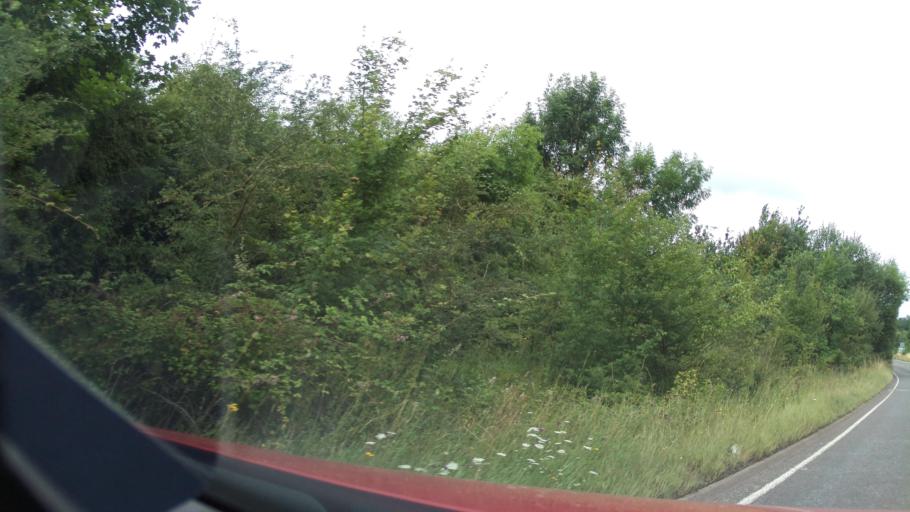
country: GB
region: England
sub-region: Northamptonshire
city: Geddington
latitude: 52.4460
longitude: -0.7351
